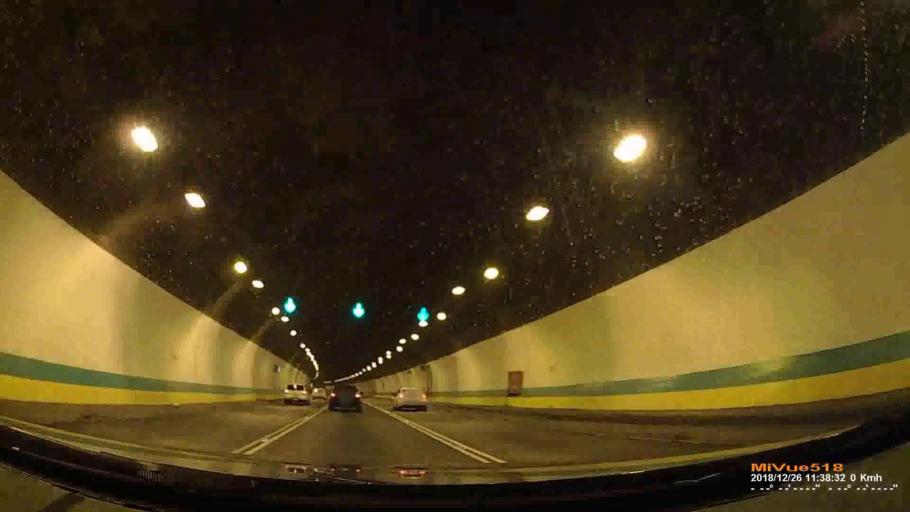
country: TW
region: Taipei
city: Taipei
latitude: 24.9813
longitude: 121.5852
